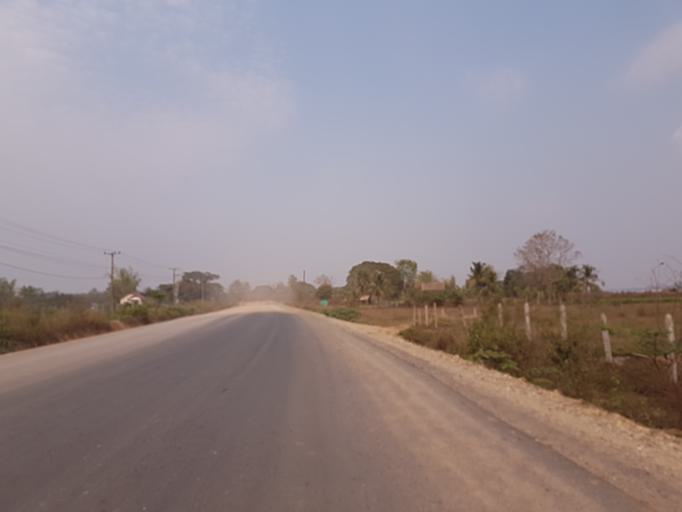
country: TH
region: Nong Khai
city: Nong Khai
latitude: 17.9722
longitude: 102.8493
